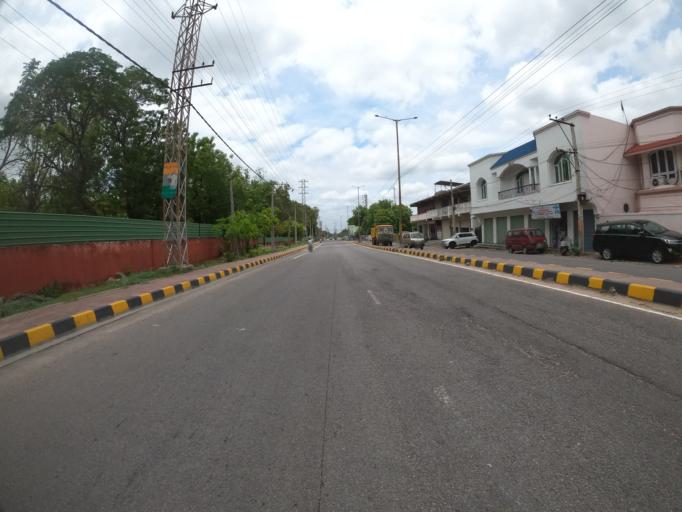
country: IN
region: Telangana
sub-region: Hyderabad
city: Hyderabad
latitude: 17.3759
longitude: 78.3935
